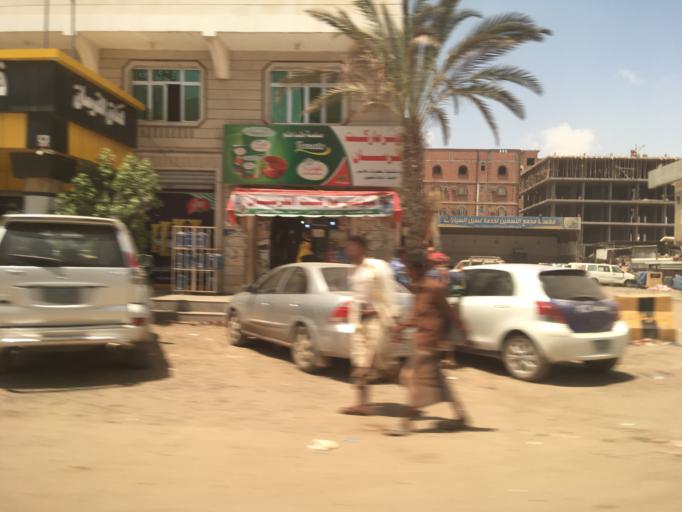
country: YE
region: Aden
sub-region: Al Mansura
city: Al Mansurah
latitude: 12.8671
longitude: 44.9707
